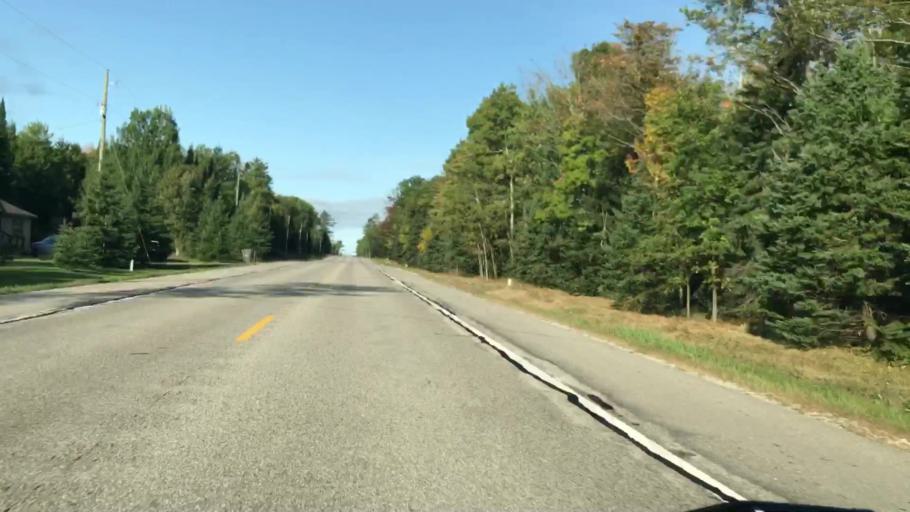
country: US
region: Michigan
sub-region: Luce County
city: Newberry
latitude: 46.3035
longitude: -85.3483
